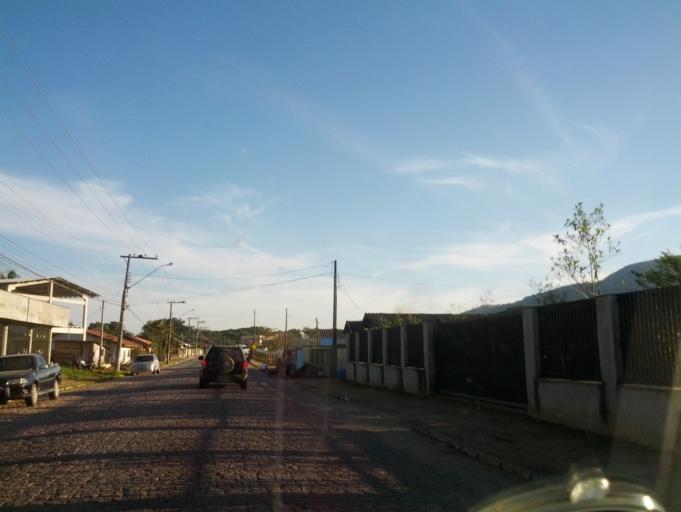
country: BR
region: Santa Catarina
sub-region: Indaial
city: Indaial
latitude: -26.9019
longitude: -49.2581
